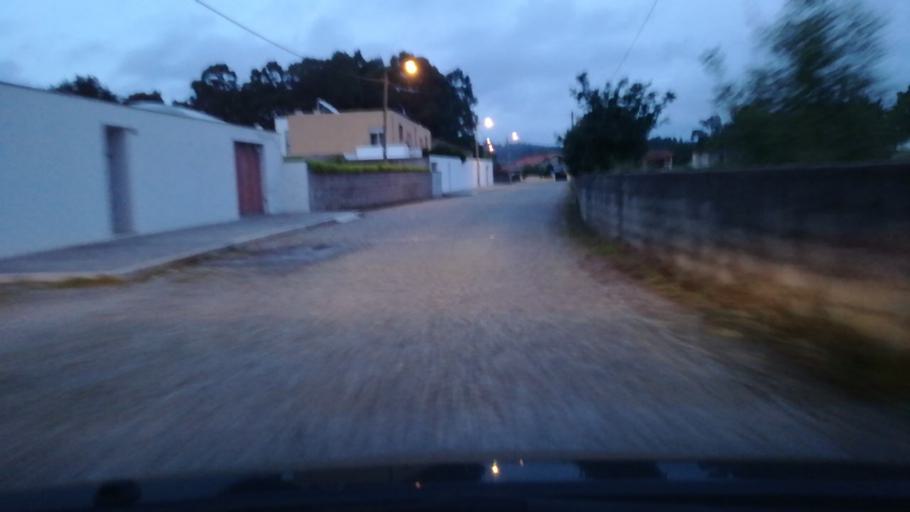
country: PT
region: Porto
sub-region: Maia
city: Anta
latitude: 41.2691
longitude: -8.6088
